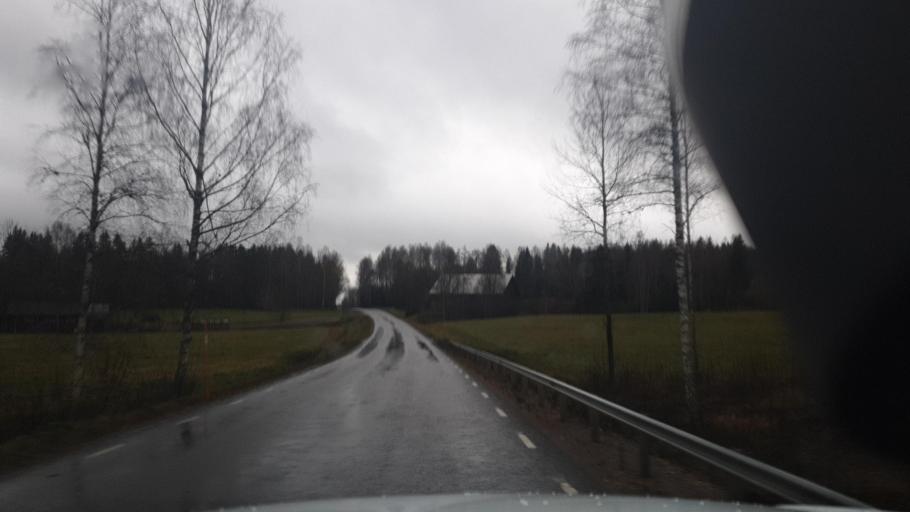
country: SE
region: Vaermland
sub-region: Eda Kommun
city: Charlottenberg
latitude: 59.7926
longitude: 12.1542
